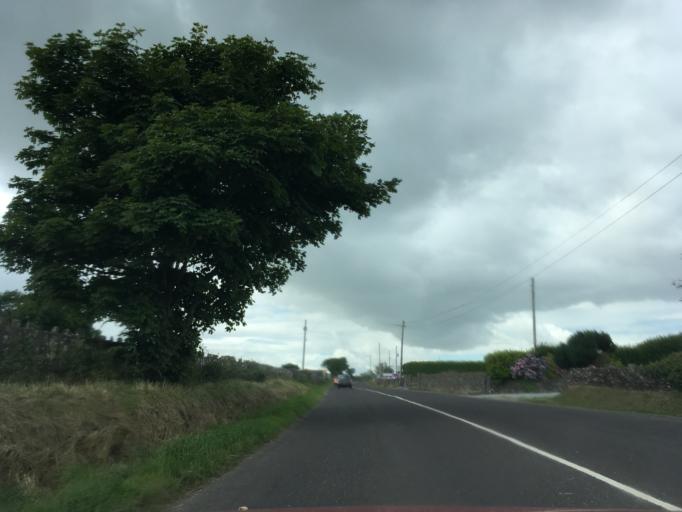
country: IE
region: Munster
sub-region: County Cork
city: Crosshaven
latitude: 51.7909
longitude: -8.3037
